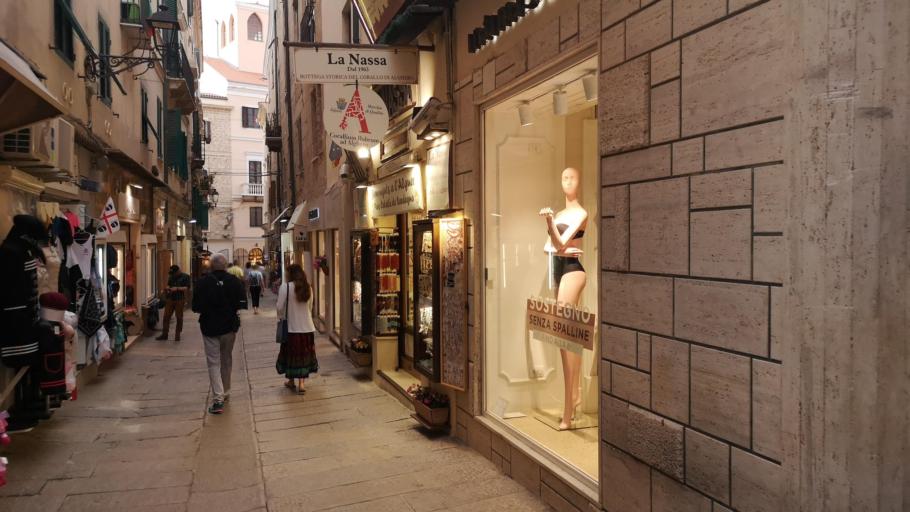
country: IT
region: Sardinia
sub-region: Provincia di Sassari
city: Alghero
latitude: 40.5588
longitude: 8.3135
